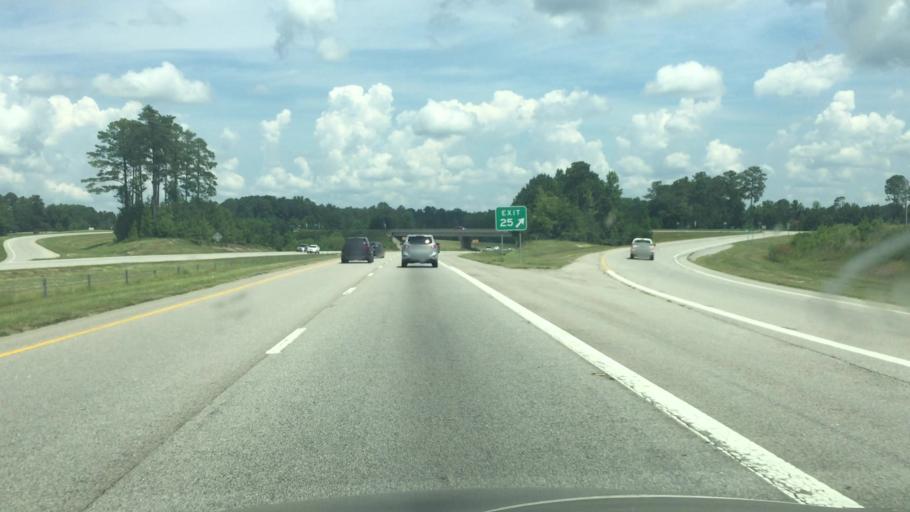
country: US
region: North Carolina
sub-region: Richmond County
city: Ellerbe
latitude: 35.0403
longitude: -79.7682
